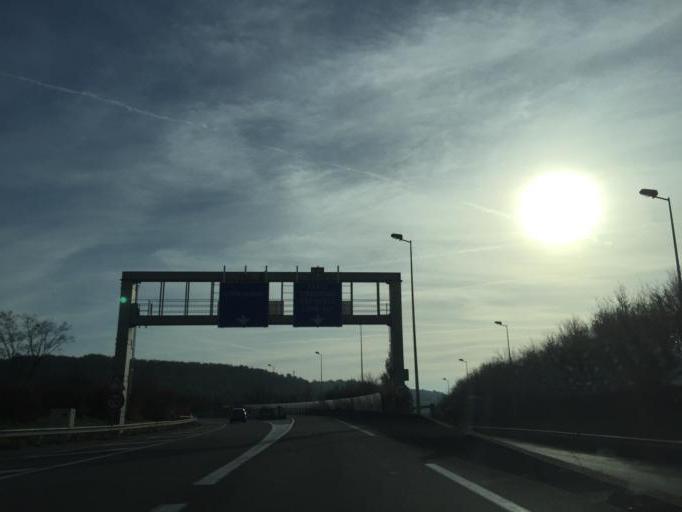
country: FR
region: Rhone-Alpes
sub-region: Departement de l'Isere
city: Chasse-sur-Rhone
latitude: 45.5881
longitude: 4.7960
